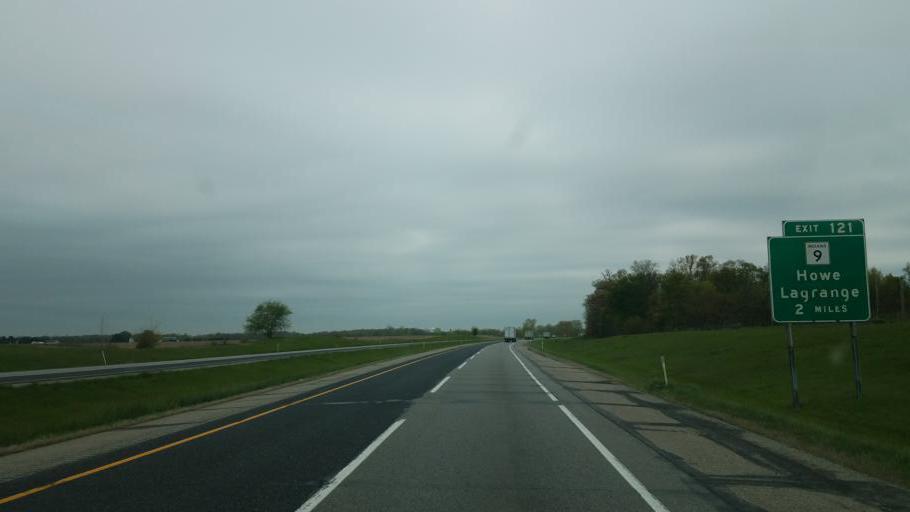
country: US
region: Michigan
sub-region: Saint Joseph County
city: Sturgis
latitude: 41.7502
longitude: -85.3884
